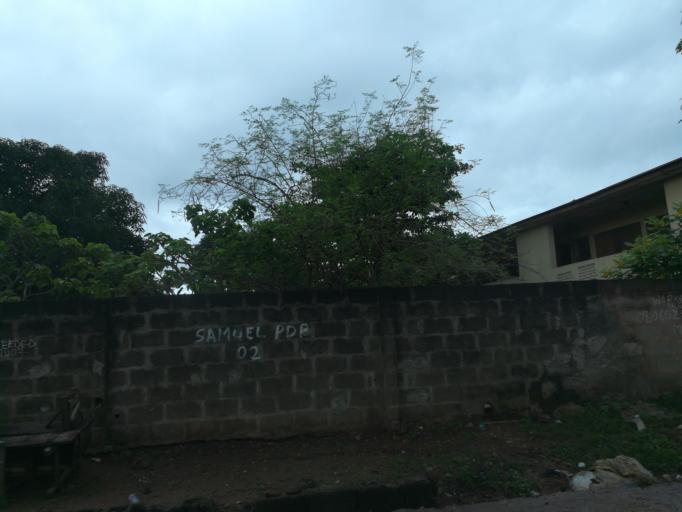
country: NG
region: Lagos
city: Agege
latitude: 6.6137
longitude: 3.3266
